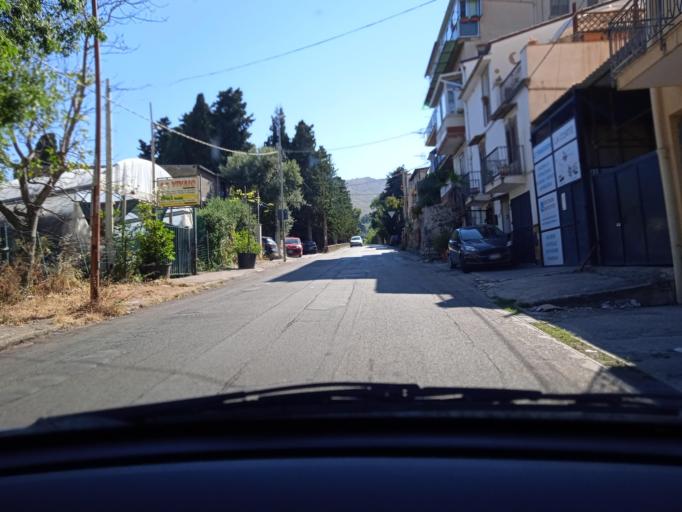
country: IT
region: Sicily
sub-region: Palermo
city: Cannizzaro-Favara
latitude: 38.0736
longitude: 13.2742
